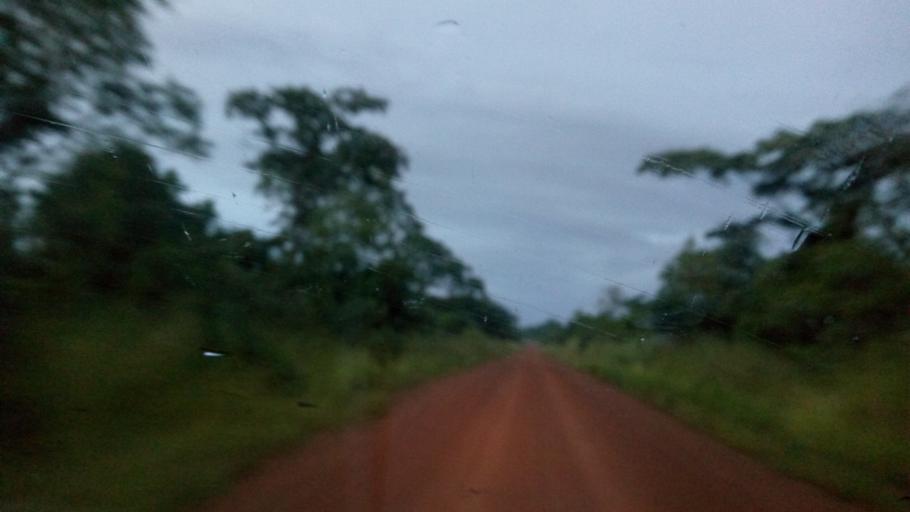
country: ZM
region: Luapula
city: Nchelenge
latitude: -9.8384
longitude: 28.1281
